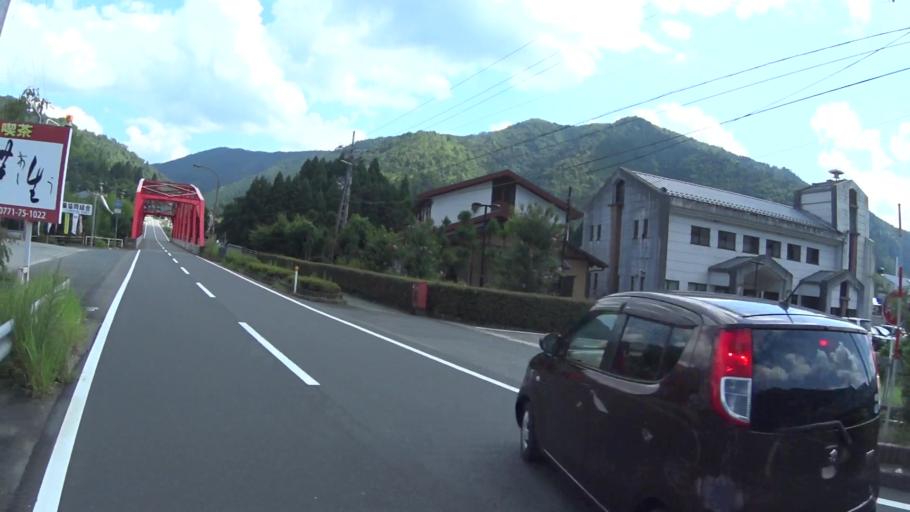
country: JP
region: Fukui
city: Obama
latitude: 35.2774
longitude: 135.5881
